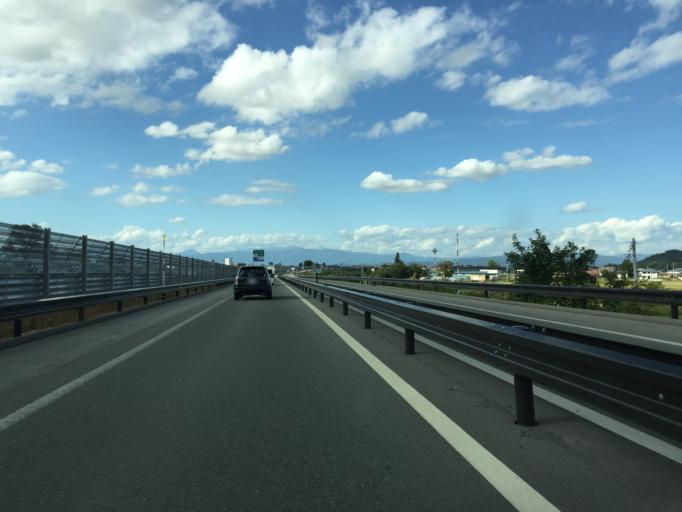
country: JP
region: Yamagata
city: Yonezawa
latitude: 37.9150
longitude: 140.1387
